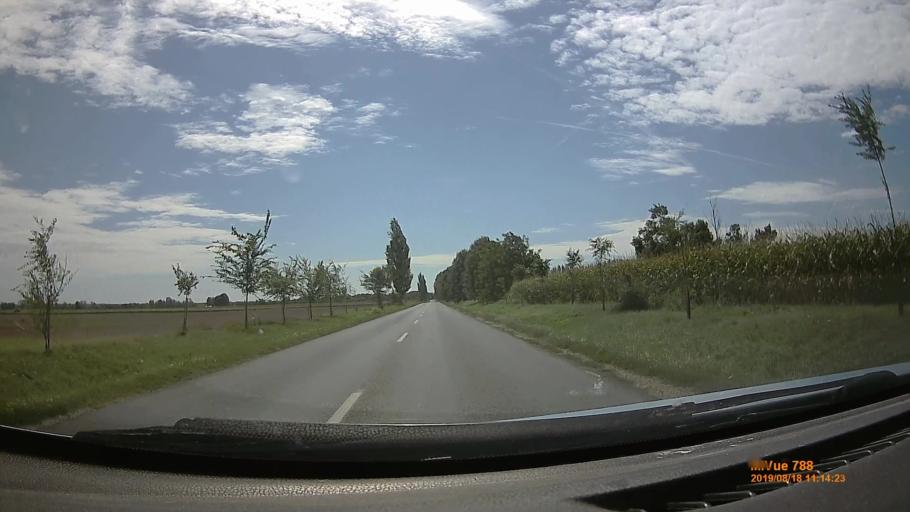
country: HU
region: Fejer
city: Szabadbattyan
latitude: 47.0920
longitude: 18.3955
